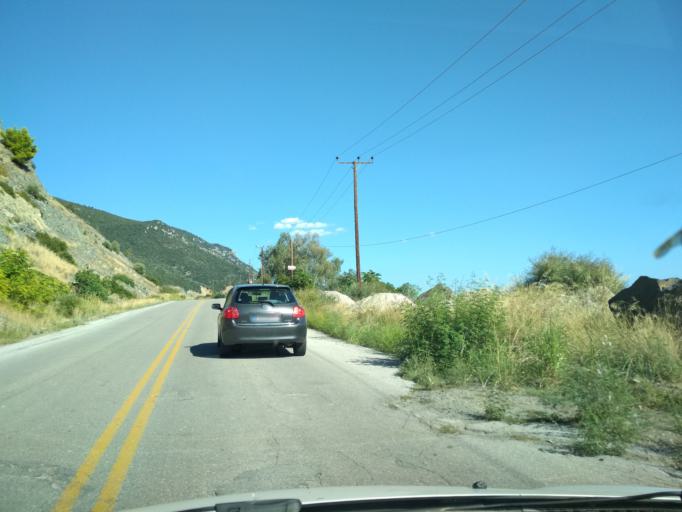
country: GR
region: Central Greece
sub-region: Nomos Evvoias
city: Oreoi
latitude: 38.8527
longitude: 23.1295
